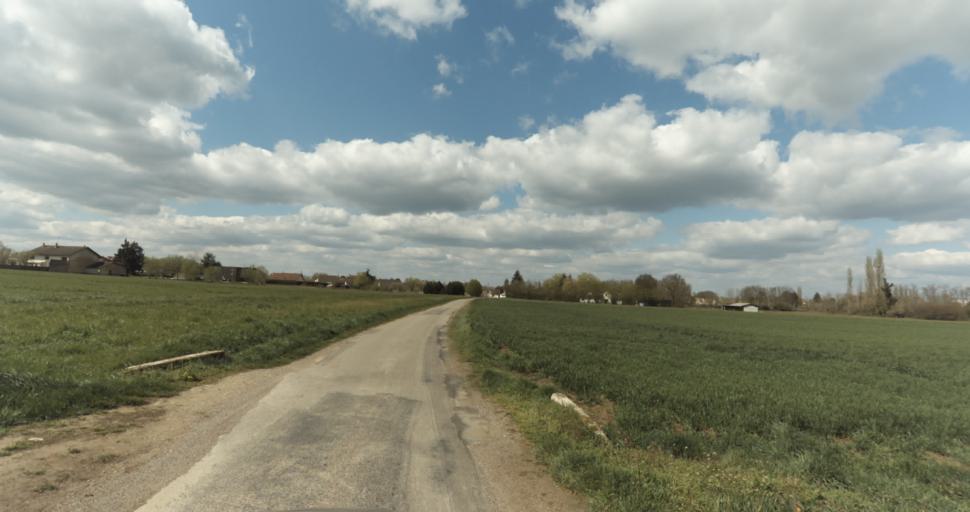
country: FR
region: Bourgogne
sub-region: Departement de la Cote-d'Or
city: Auxonne
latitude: 47.1870
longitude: 5.4096
